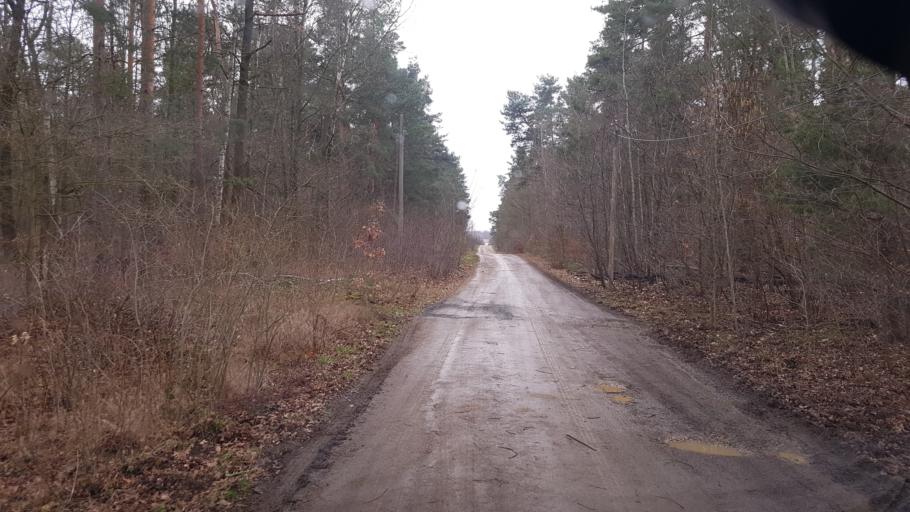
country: DE
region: Brandenburg
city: Crinitz
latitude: 51.7459
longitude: 13.7687
